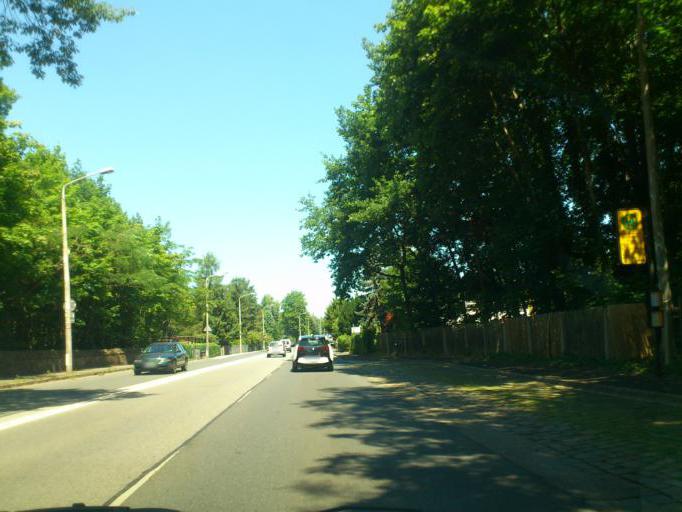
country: DE
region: Saxony
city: Albertstadt
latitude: 51.0912
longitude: 13.7379
